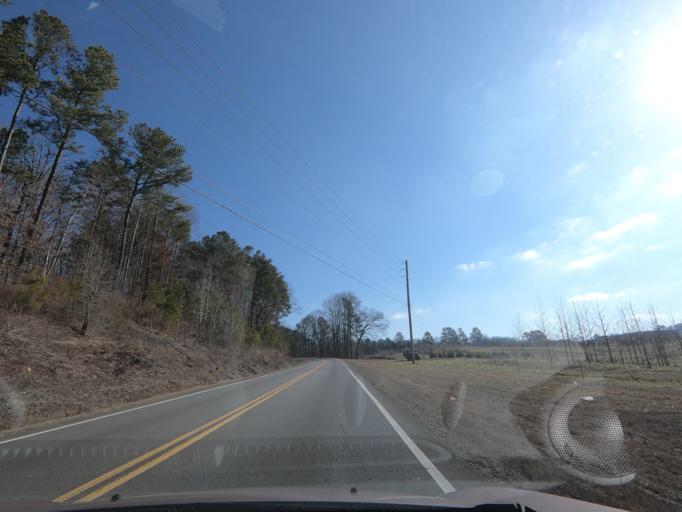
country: US
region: Georgia
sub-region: Cherokee County
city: Ball Ground
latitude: 34.2896
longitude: -84.2721
